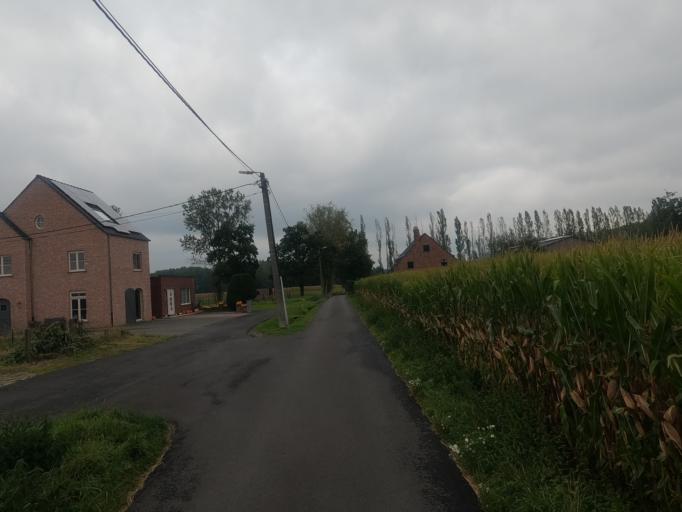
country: BE
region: Flanders
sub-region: Provincie Antwerpen
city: Berlaar
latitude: 51.1209
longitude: 4.6445
